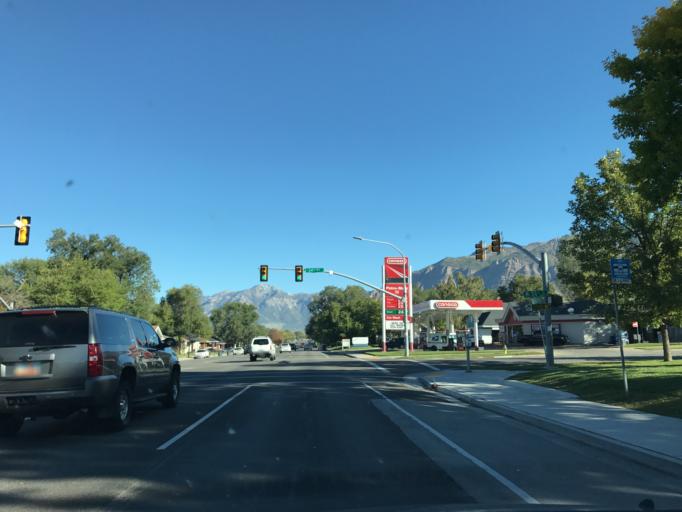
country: US
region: Utah
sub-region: Weber County
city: Ogden
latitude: 41.2221
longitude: -111.9481
